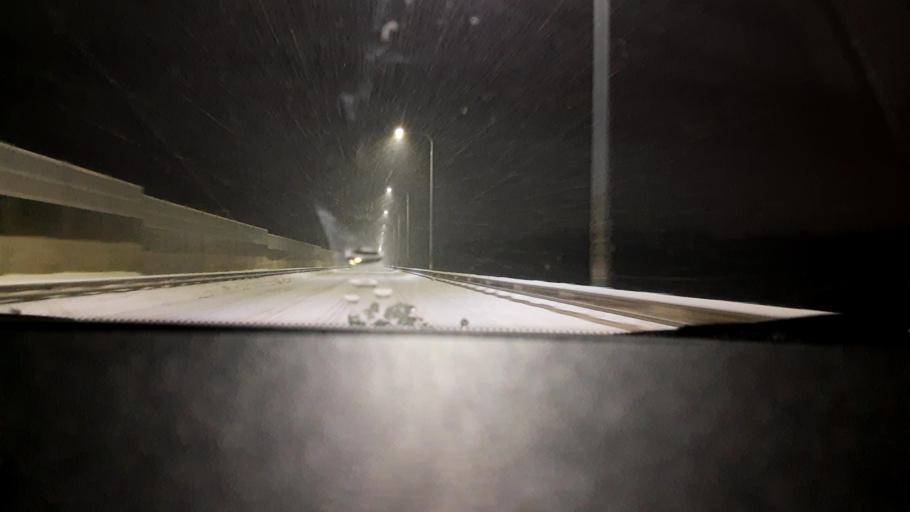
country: RU
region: Nizjnij Novgorod
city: Neklyudovo
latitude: 56.4277
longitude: 43.9687
